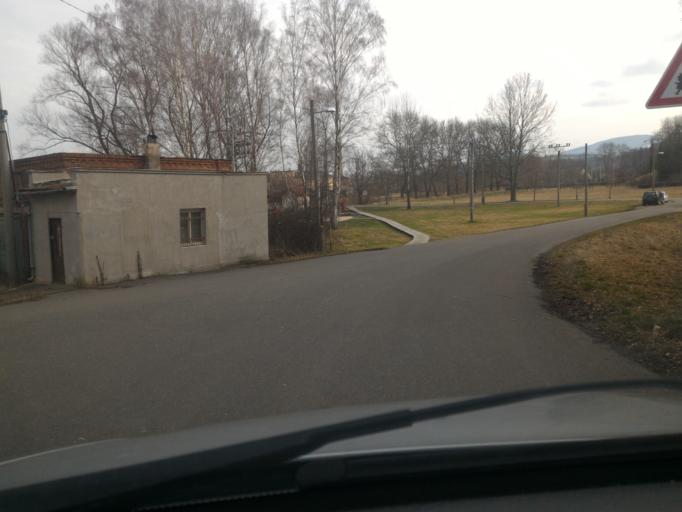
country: CZ
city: Hradek nad Nisou
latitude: 50.8549
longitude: 14.8220
